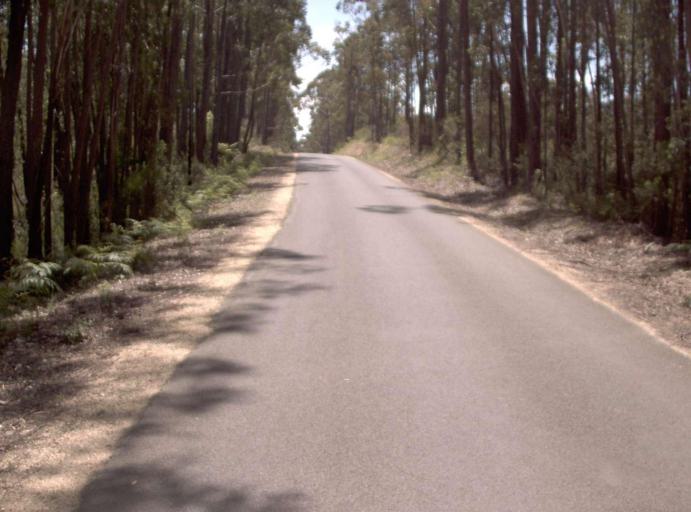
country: AU
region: New South Wales
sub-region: Bombala
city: Bombala
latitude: -37.5694
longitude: 148.9439
